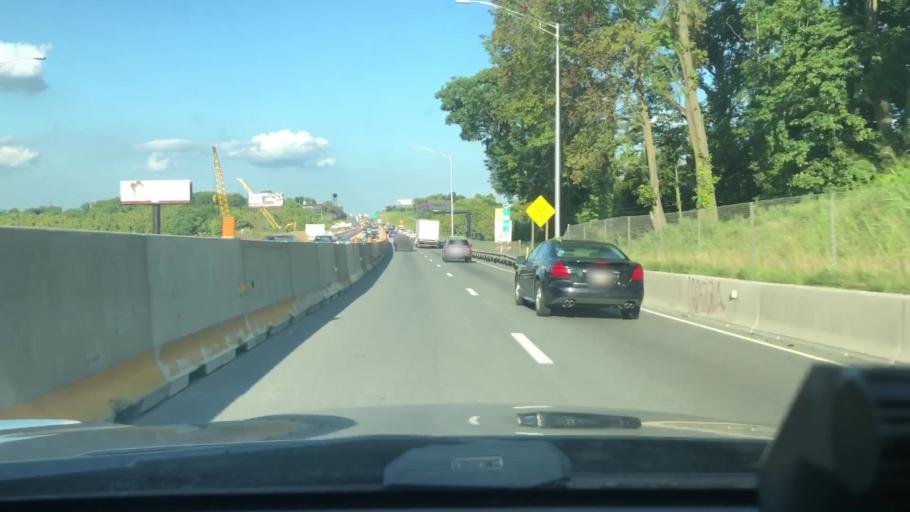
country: US
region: Pennsylvania
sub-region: Lehigh County
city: Fullerton
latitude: 40.6337
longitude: -75.4708
